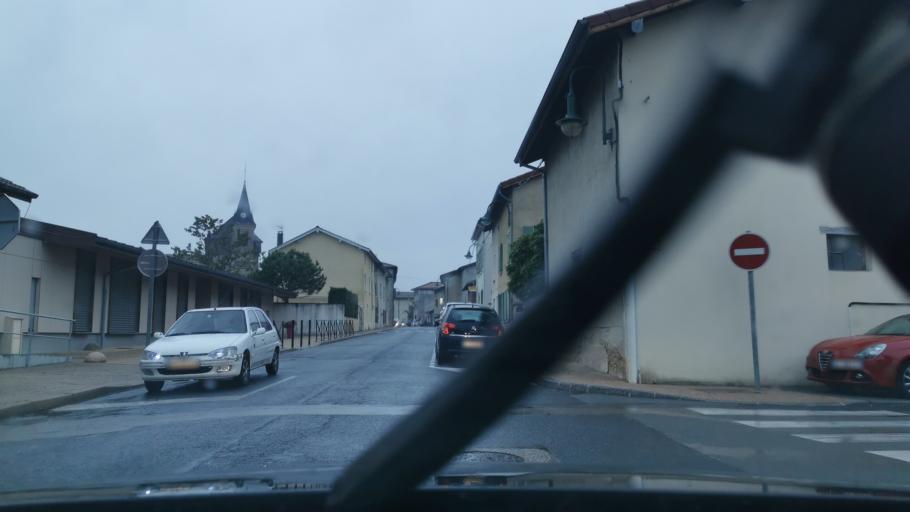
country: FR
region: Rhone-Alpes
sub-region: Departement de l'Ain
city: Amberieux-en-Dombes
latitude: 45.9958
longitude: 4.9033
